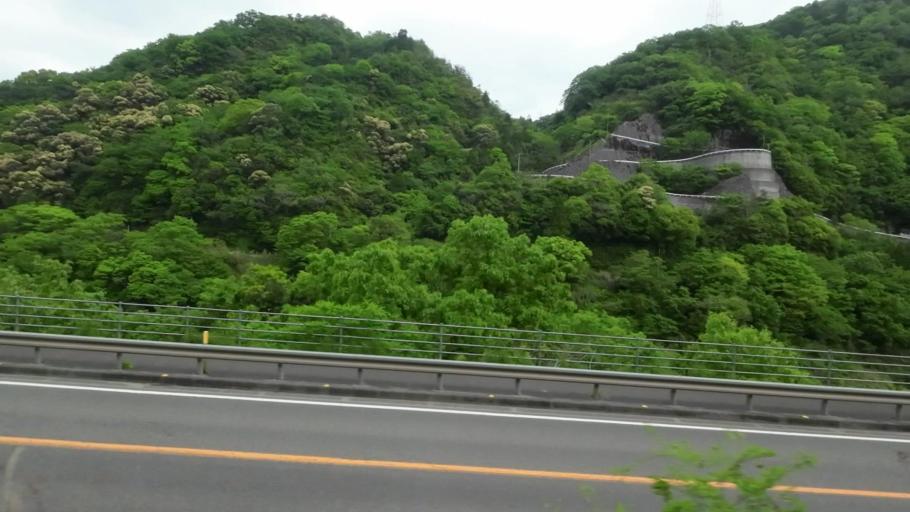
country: JP
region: Tokushima
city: Ikedacho
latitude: 33.9806
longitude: 133.7850
